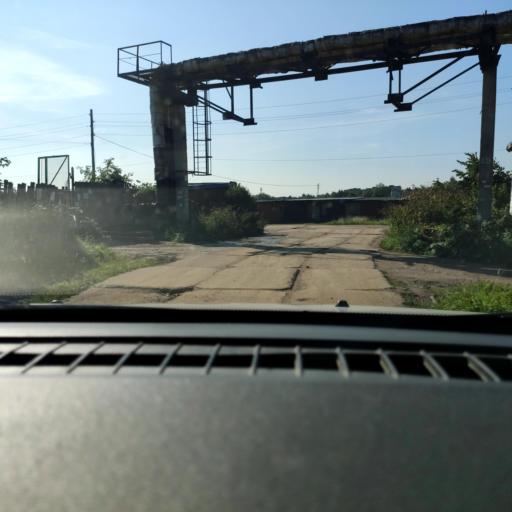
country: RU
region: Perm
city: Novyye Lyady
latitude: 58.0557
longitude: 56.5830
